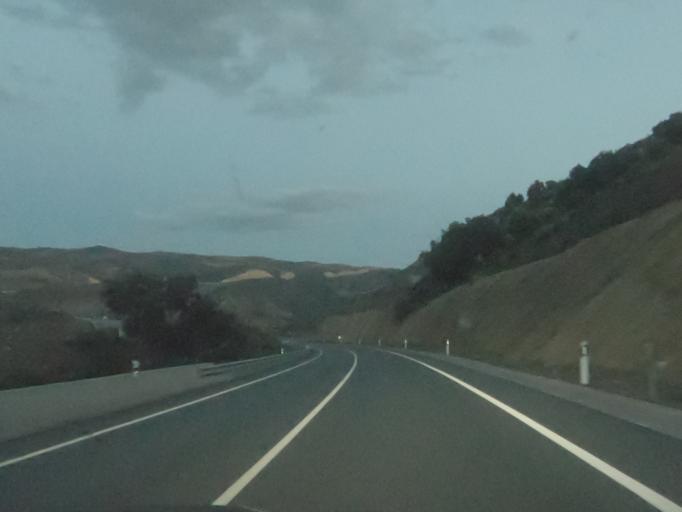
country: PT
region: Braganca
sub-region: Alfandega da Fe
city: Alfandega da Fe
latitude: 41.3090
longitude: -6.9245
